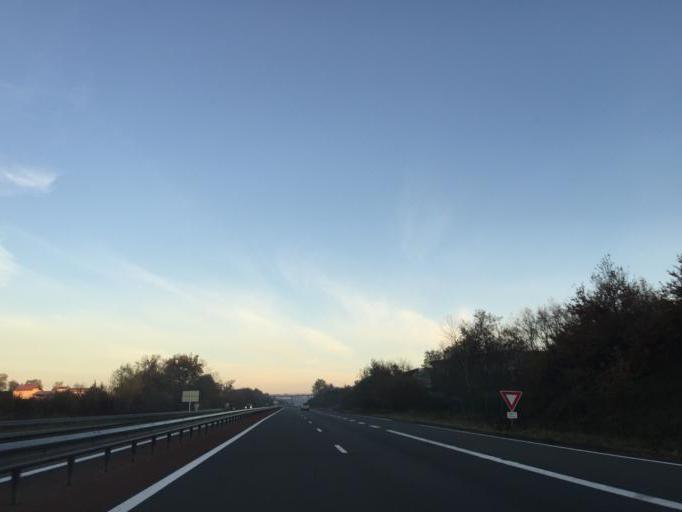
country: FR
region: Rhone-Alpes
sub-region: Departement de la Loire
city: Neulise
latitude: 45.8856
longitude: 4.1766
